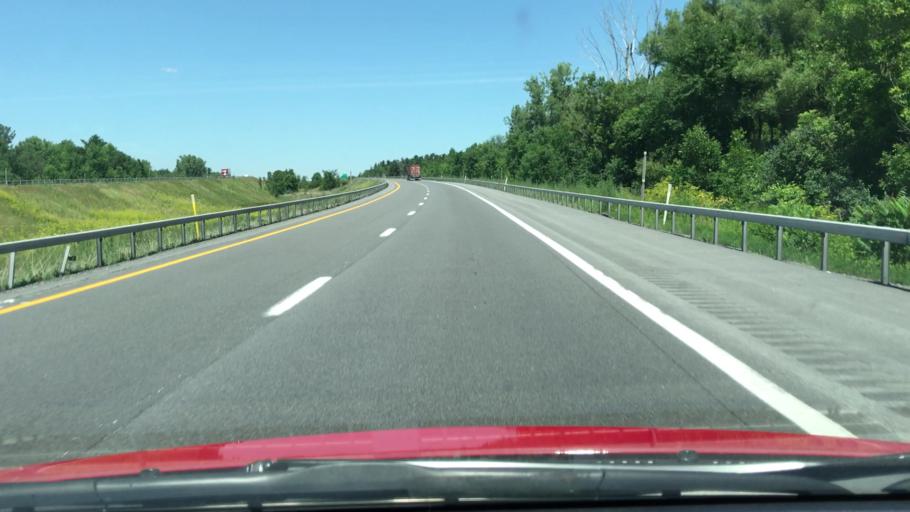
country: US
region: New York
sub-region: Clinton County
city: Champlain
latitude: 44.8801
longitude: -73.4509
